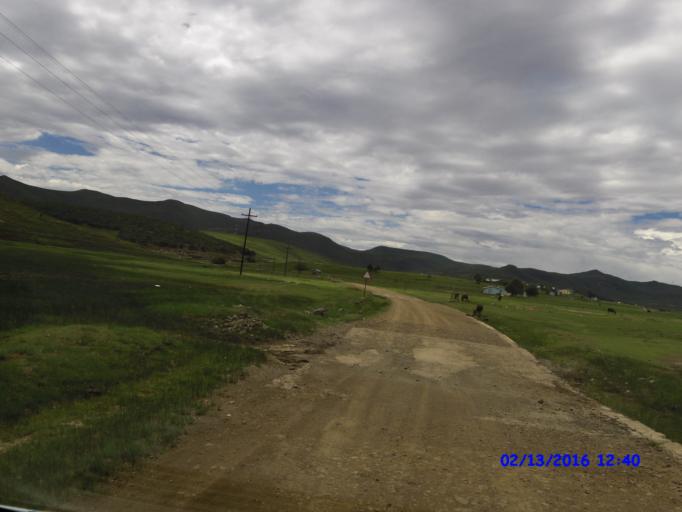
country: LS
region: Maseru
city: Nako
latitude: -29.8315
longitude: 28.0324
